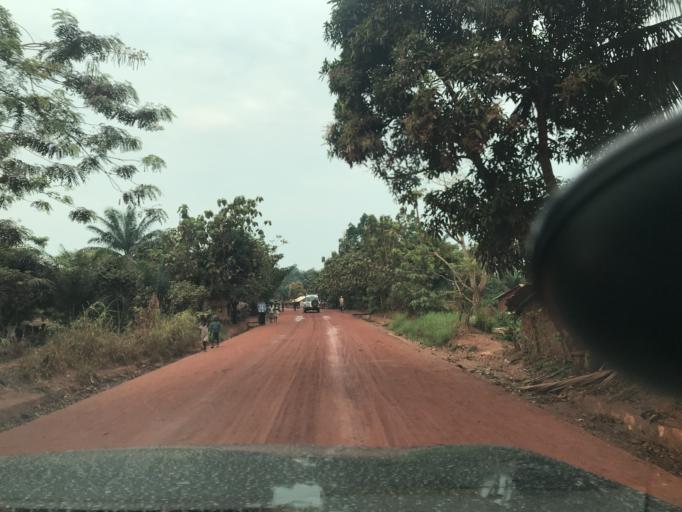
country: CD
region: Equateur
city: Gemena
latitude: 3.2268
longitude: 19.7762
